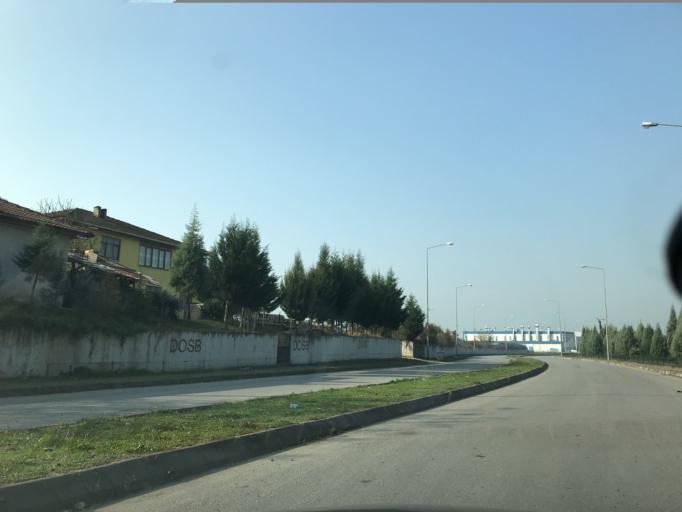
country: TR
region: Duzce
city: Duzce
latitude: 40.7832
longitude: 31.1530
